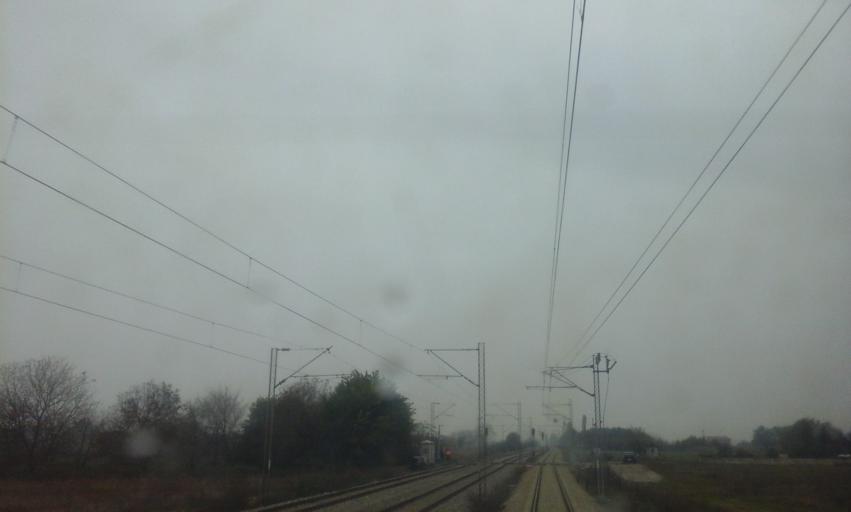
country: RS
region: Central Serbia
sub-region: Pomoravski Okrug
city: Paracin
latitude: 43.8734
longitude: 21.3926
